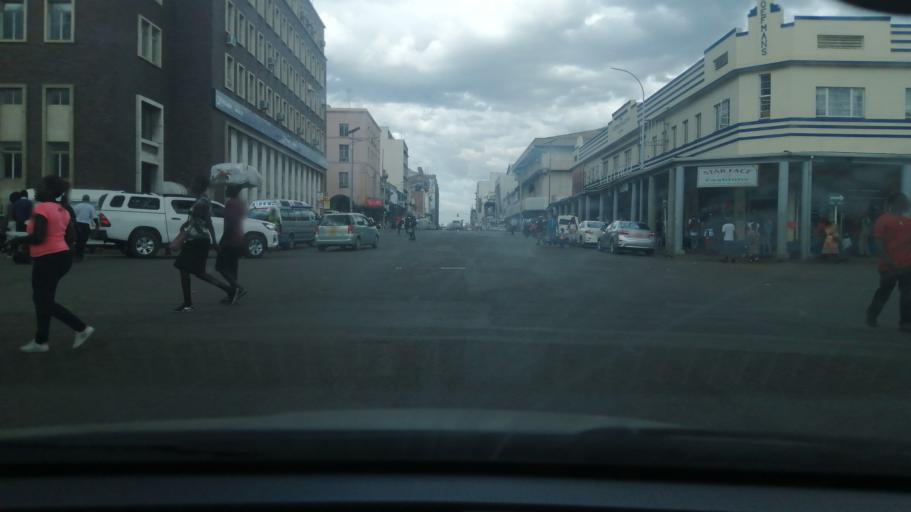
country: ZW
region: Harare
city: Harare
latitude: -17.8329
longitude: 31.0480
